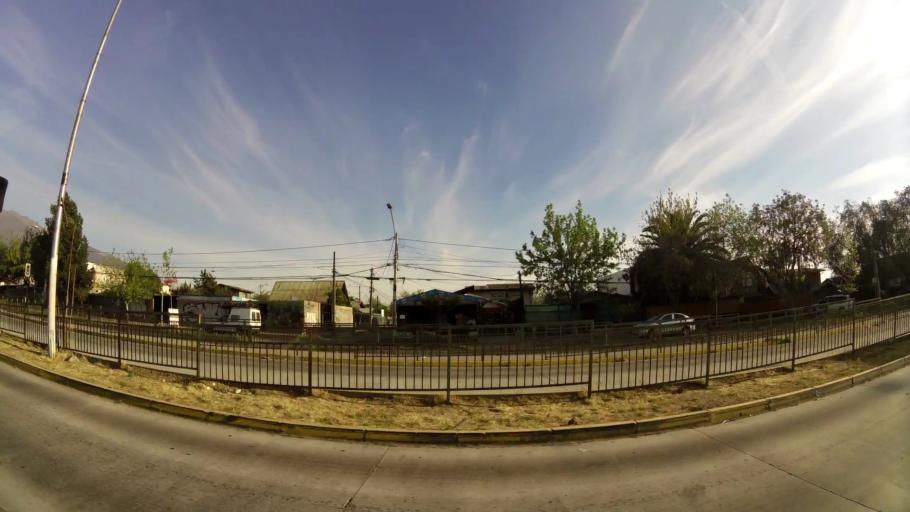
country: CL
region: Santiago Metropolitan
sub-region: Provincia de Santiago
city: Villa Presidente Frei, Nunoa, Santiago, Chile
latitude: -33.4727
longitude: -70.5582
